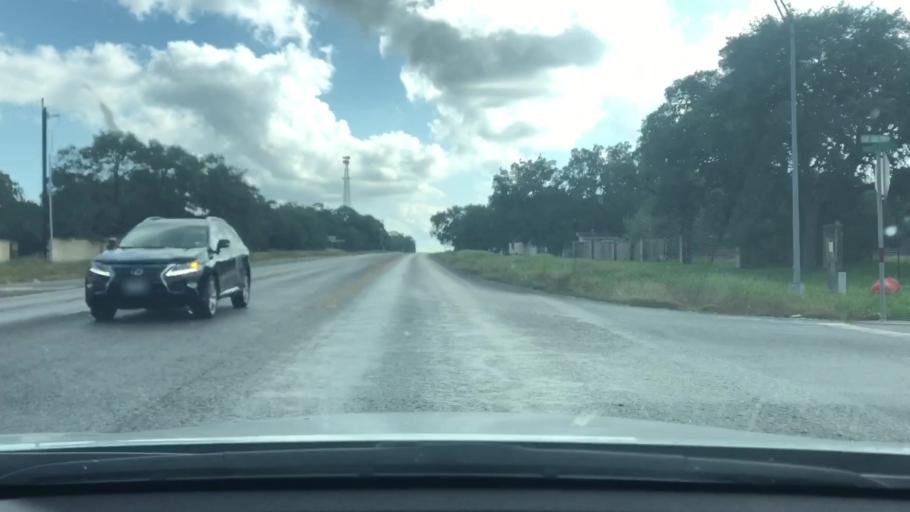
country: US
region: Texas
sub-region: Bexar County
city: Fair Oaks Ranch
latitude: 29.7388
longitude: -98.6233
